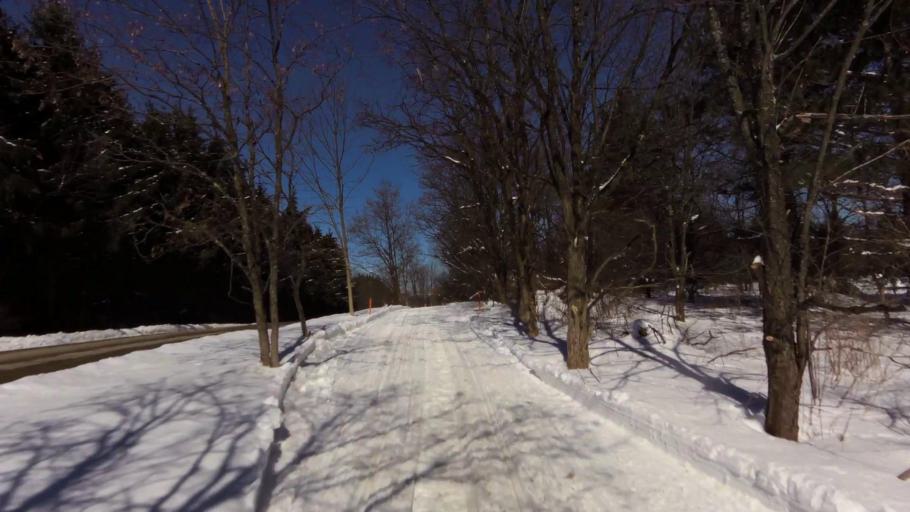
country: US
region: New York
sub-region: Allegany County
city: Houghton
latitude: 42.4168
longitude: -78.3083
